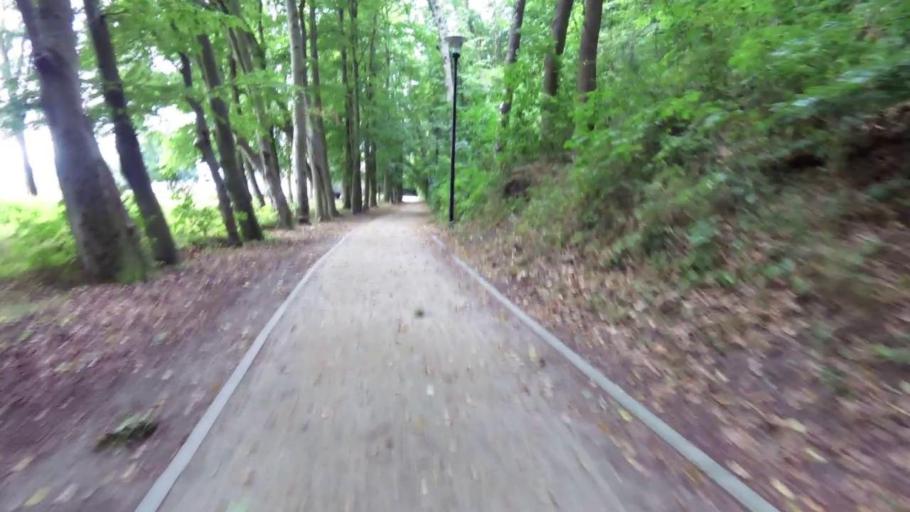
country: PL
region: West Pomeranian Voivodeship
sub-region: Powiat choszczenski
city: Choszczno
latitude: 53.1586
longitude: 15.4280
